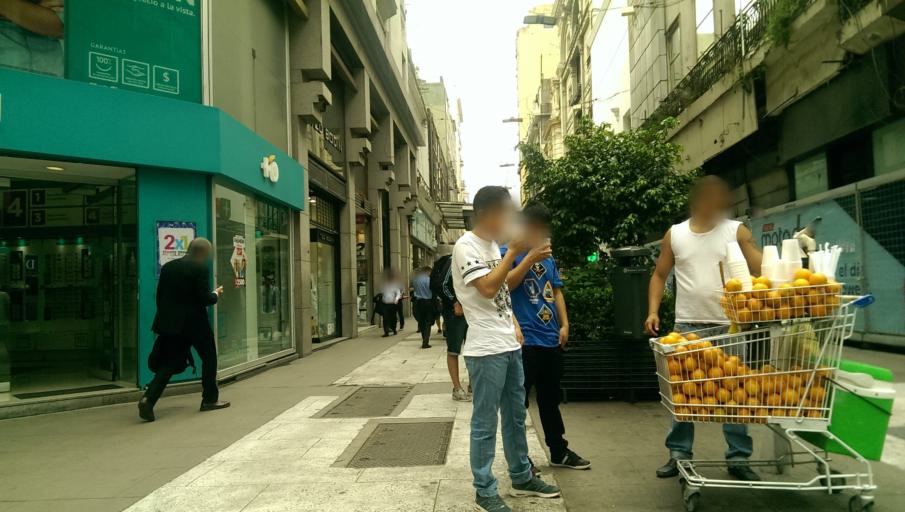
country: AR
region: Buenos Aires F.D.
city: Buenos Aires
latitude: -34.6018
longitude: -58.3752
